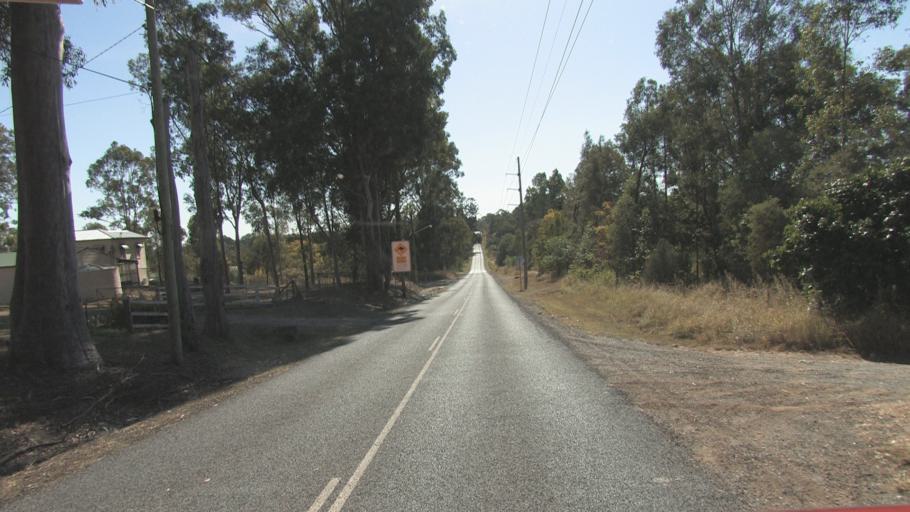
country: AU
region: Queensland
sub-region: Logan
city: Cedar Vale
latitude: -27.8758
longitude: 153.0166
